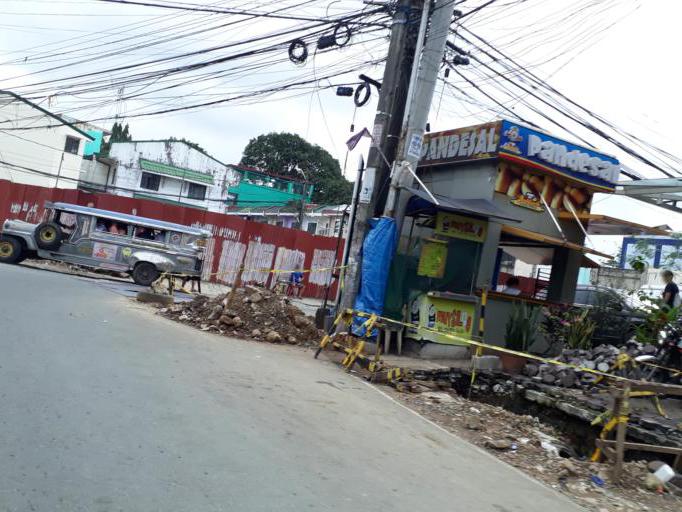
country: PH
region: Metro Manila
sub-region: San Juan
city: San Juan
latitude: 14.6175
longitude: 121.0447
